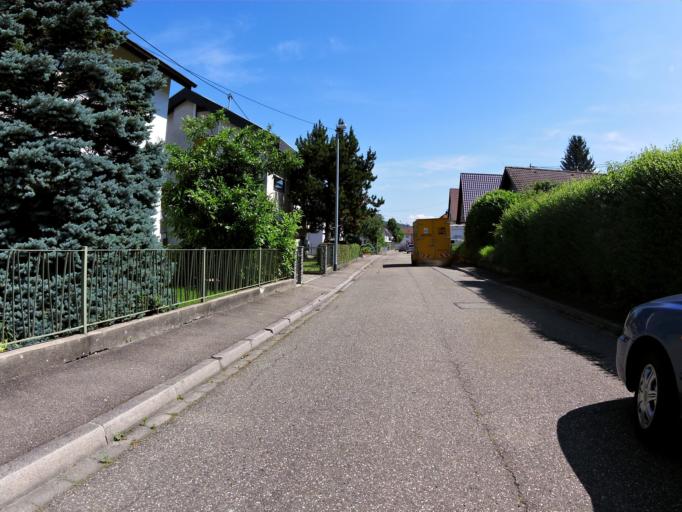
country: DE
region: Baden-Wuerttemberg
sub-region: Freiburg Region
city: Lahr
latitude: 48.3294
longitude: 7.8441
